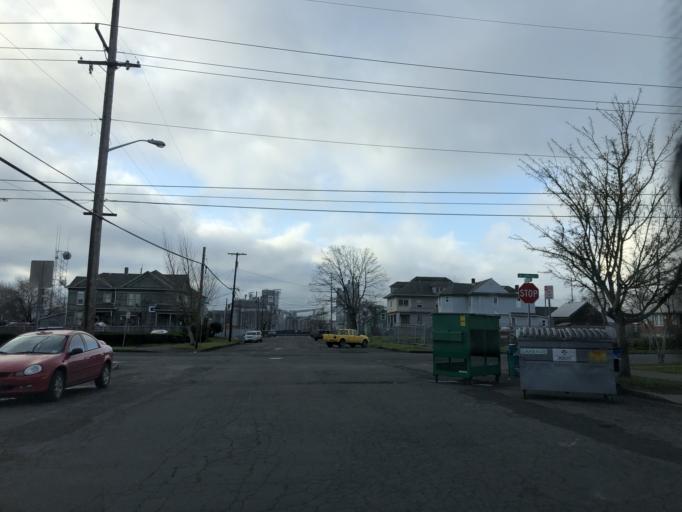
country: US
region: Washington
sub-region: Clark County
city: Vancouver
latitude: 45.6302
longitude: -122.6810
